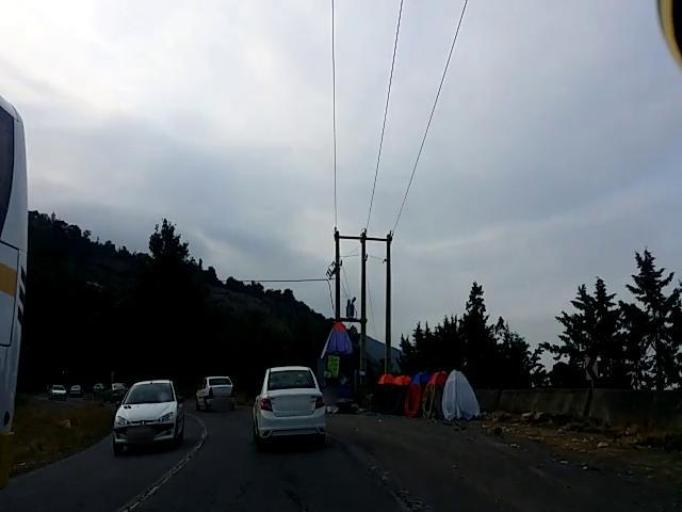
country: IR
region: Mazandaran
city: Chalus
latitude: 36.3926
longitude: 51.2750
